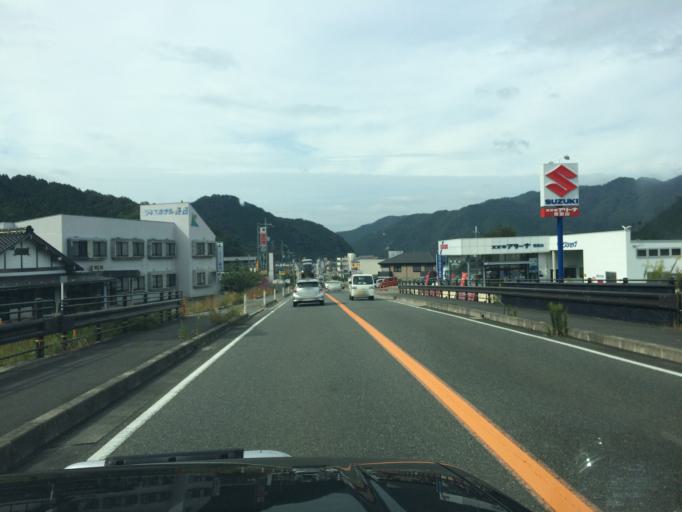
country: JP
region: Hyogo
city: Toyooka
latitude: 35.3411
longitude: 134.8430
